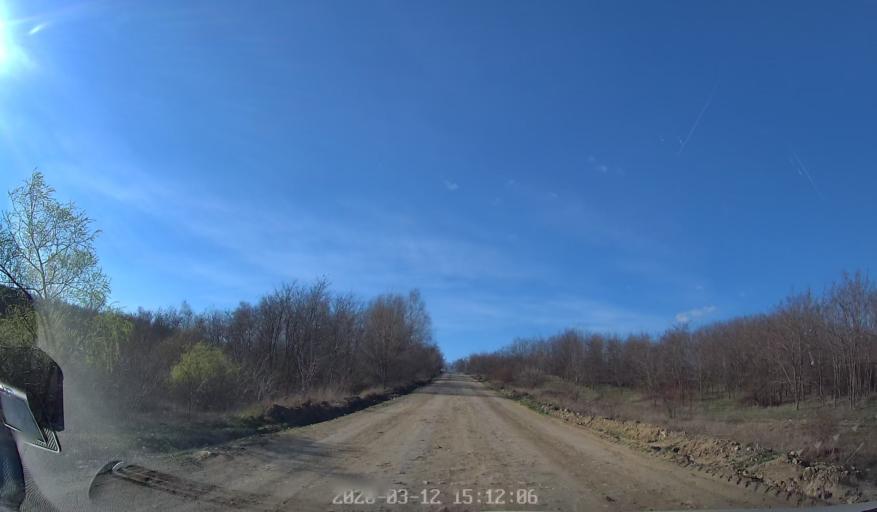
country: MD
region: Chisinau
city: Ciorescu
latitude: 47.2283
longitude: 28.9727
